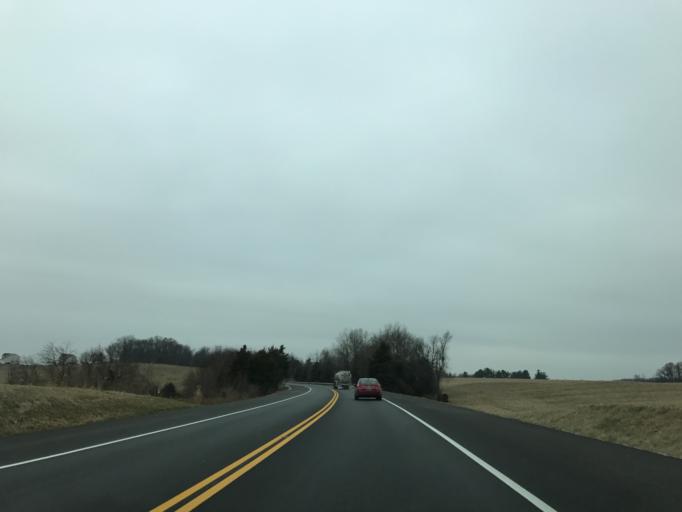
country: US
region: Maryland
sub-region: Carroll County
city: New Windsor
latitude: 39.6162
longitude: -77.0827
